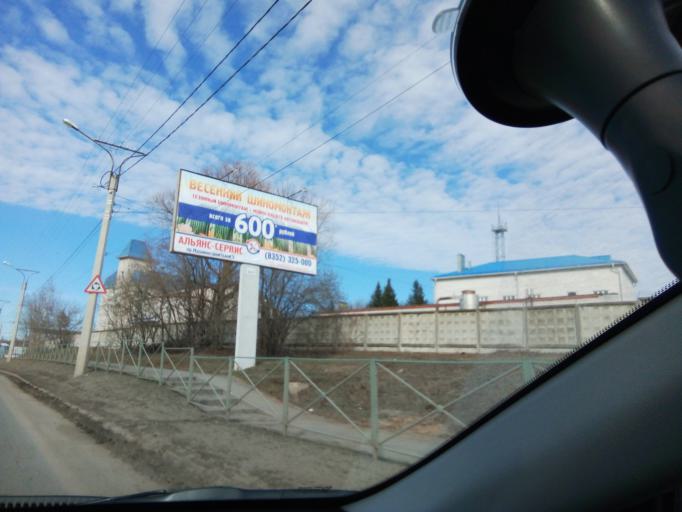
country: RU
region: Chuvashia
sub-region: Cheboksarskiy Rayon
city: Cheboksary
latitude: 56.1105
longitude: 47.2471
